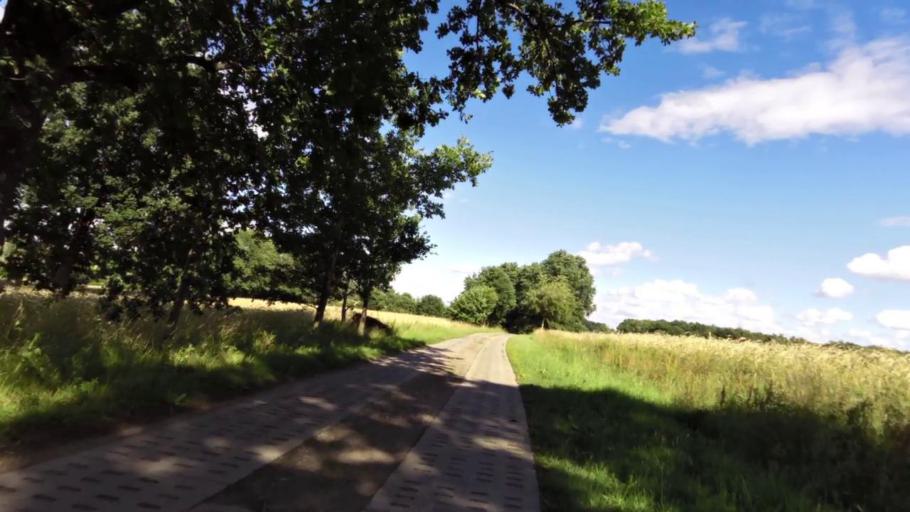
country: PL
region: West Pomeranian Voivodeship
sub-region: Powiat slawienski
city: Slawno
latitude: 54.4636
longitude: 16.7170
